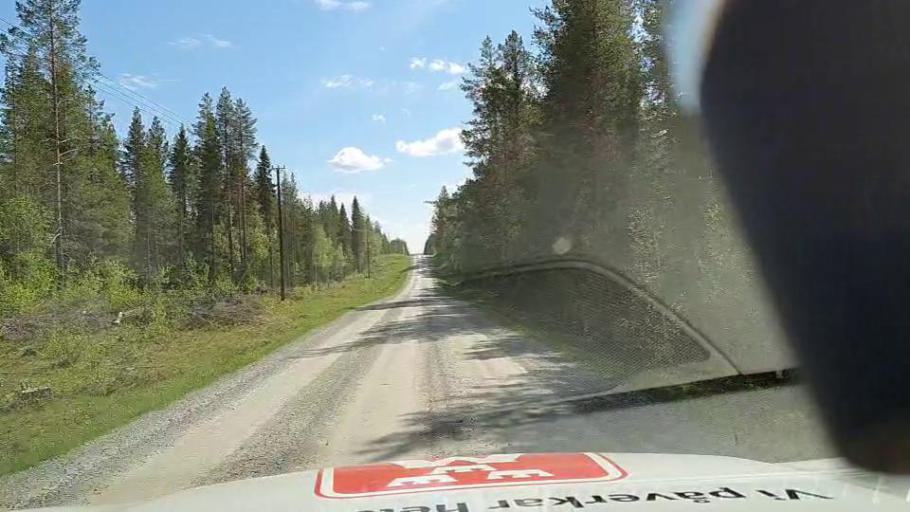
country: SE
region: Jaemtland
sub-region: Stroemsunds Kommun
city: Stroemsund
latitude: 64.4806
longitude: 15.5925
